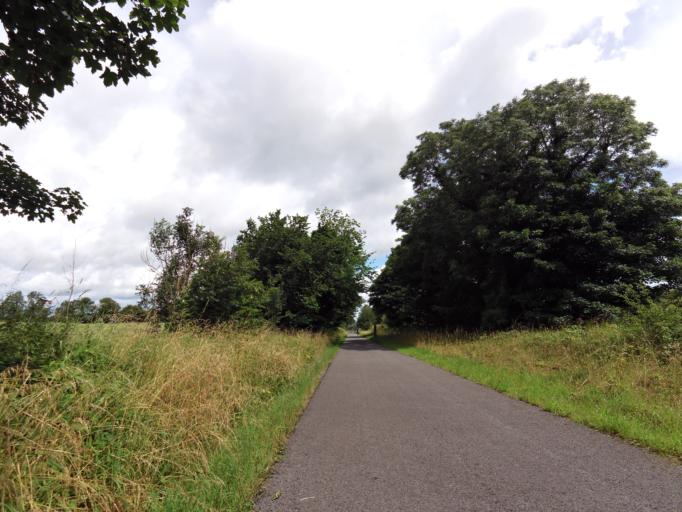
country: IE
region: Leinster
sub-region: An Iarmhi
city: Kilbeggan
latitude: 53.4649
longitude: -7.5032
